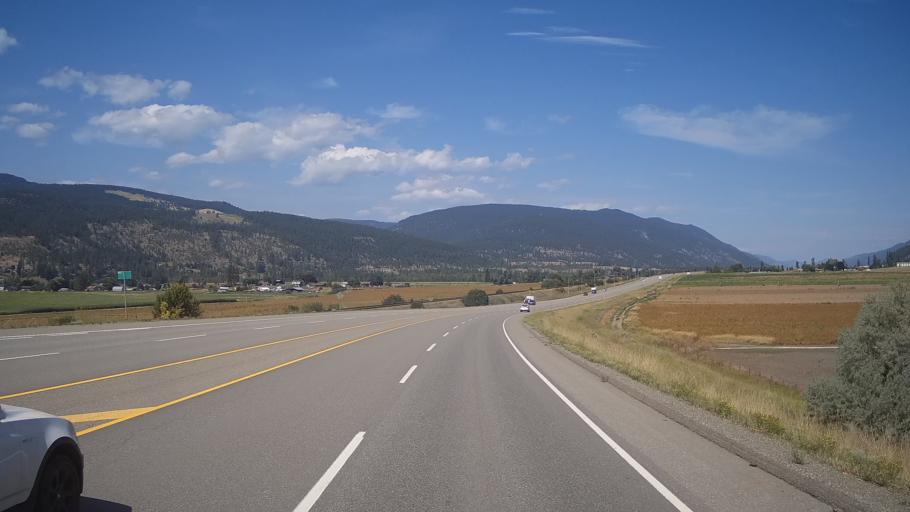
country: CA
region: British Columbia
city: Kamloops
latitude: 50.8473
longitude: -120.2732
